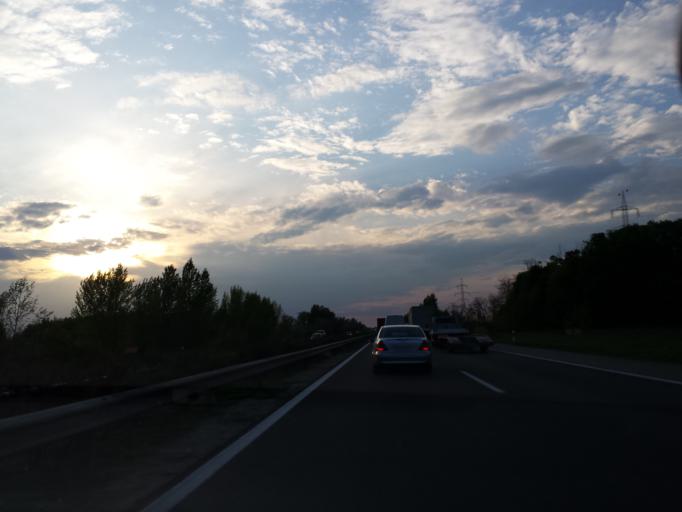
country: HU
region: Gyor-Moson-Sopron
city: Gyor
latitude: 47.6590
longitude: 17.5883
